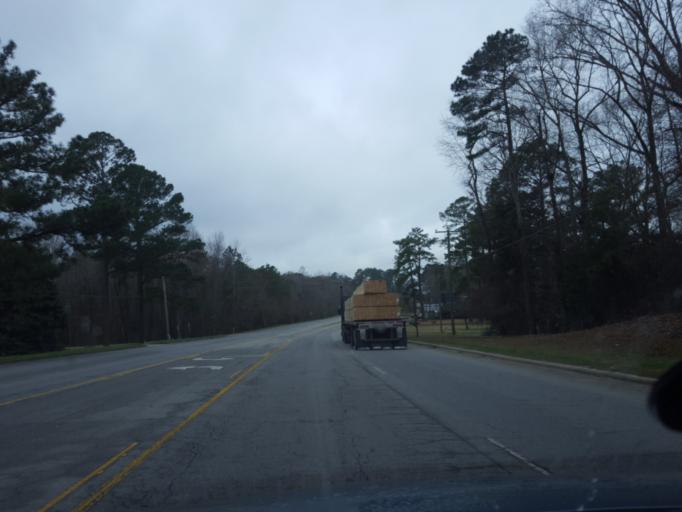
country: US
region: North Carolina
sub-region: Washington County
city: Plymouth
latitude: 35.8300
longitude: -76.7793
